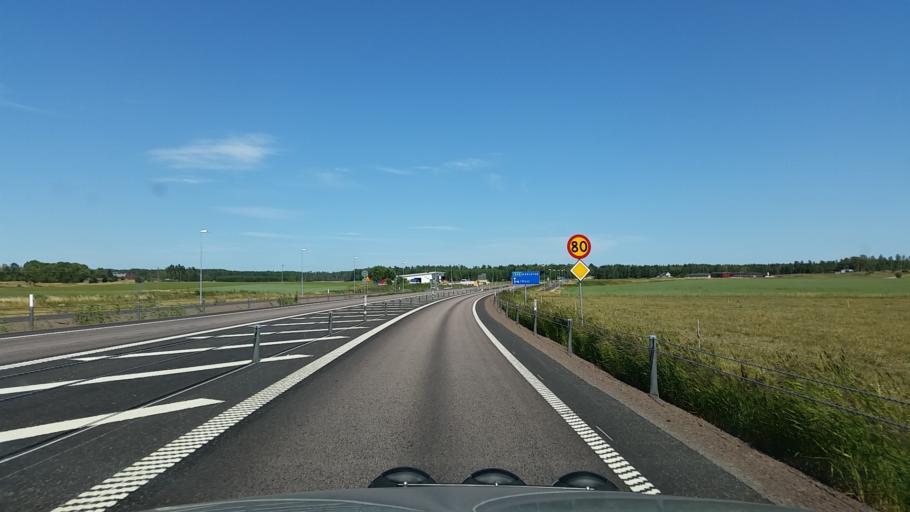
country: SE
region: Vaestra Goetaland
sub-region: Amals Kommun
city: Amal
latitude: 58.9740
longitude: 12.6240
